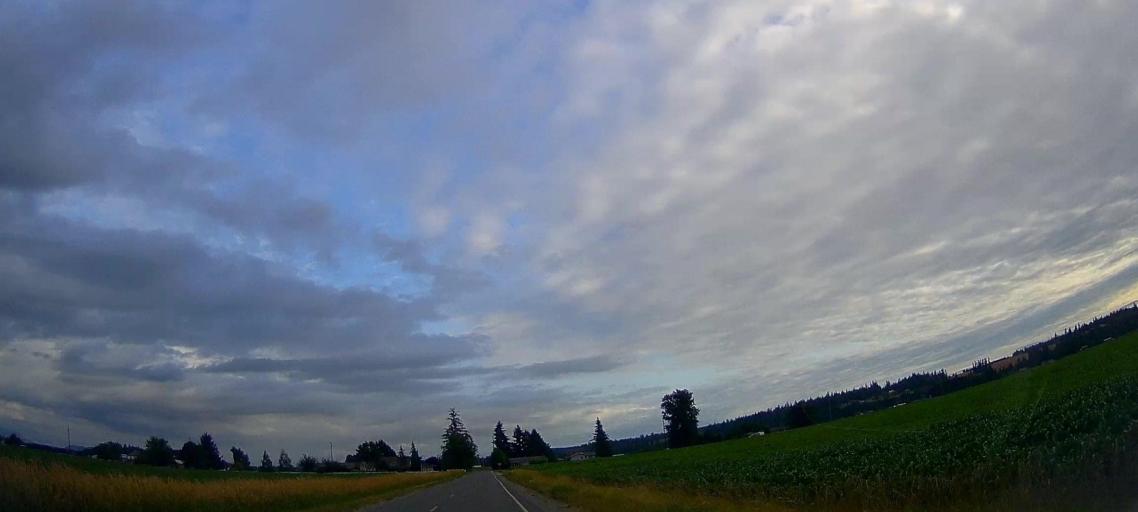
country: US
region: Washington
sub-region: Skagit County
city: Burlington
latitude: 48.5190
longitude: -122.4112
